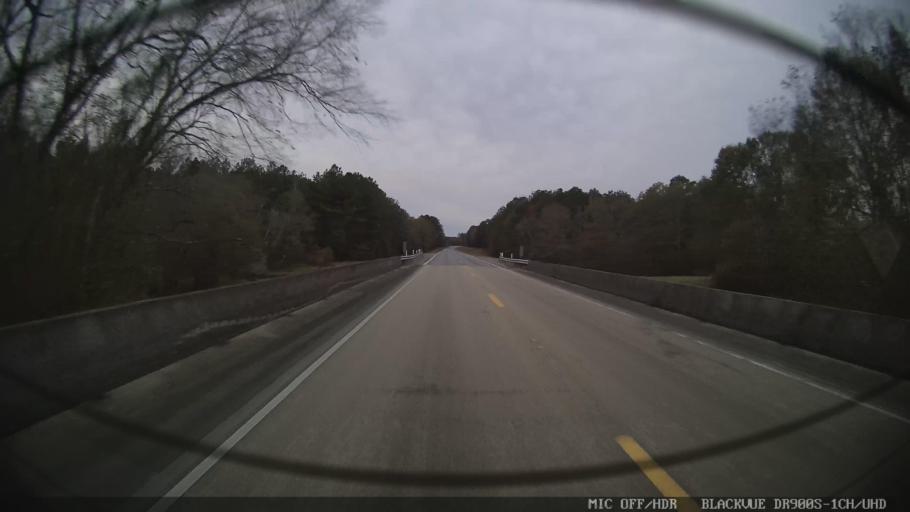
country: US
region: Mississippi
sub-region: Clarke County
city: Quitman
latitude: 32.0264
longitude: -88.8384
